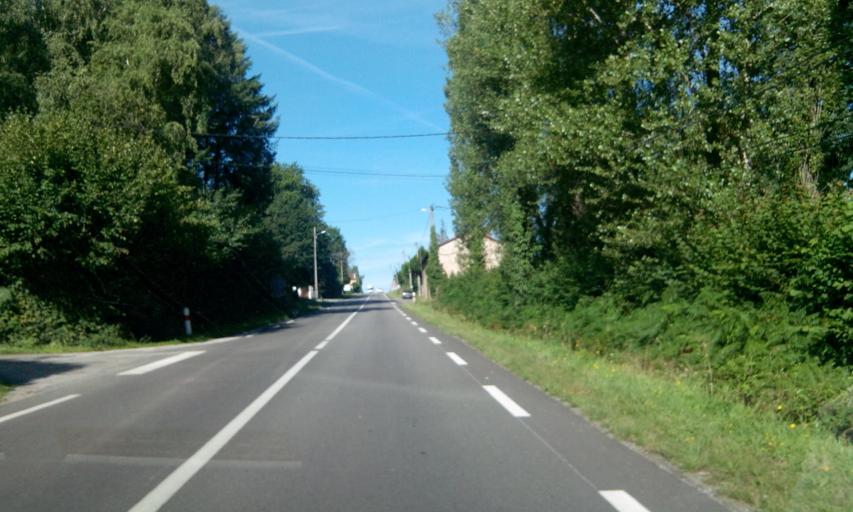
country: FR
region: Limousin
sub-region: Departement de la Haute-Vienne
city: Saint-Just-le-Martel
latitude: 45.8460
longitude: 1.4216
